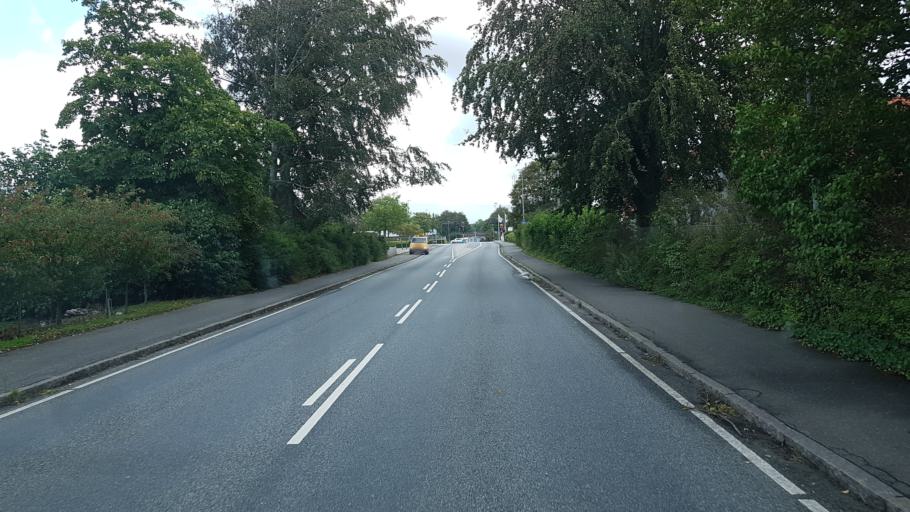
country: DK
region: South Denmark
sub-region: Vejen Kommune
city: Vejen
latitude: 55.4707
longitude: 9.1420
